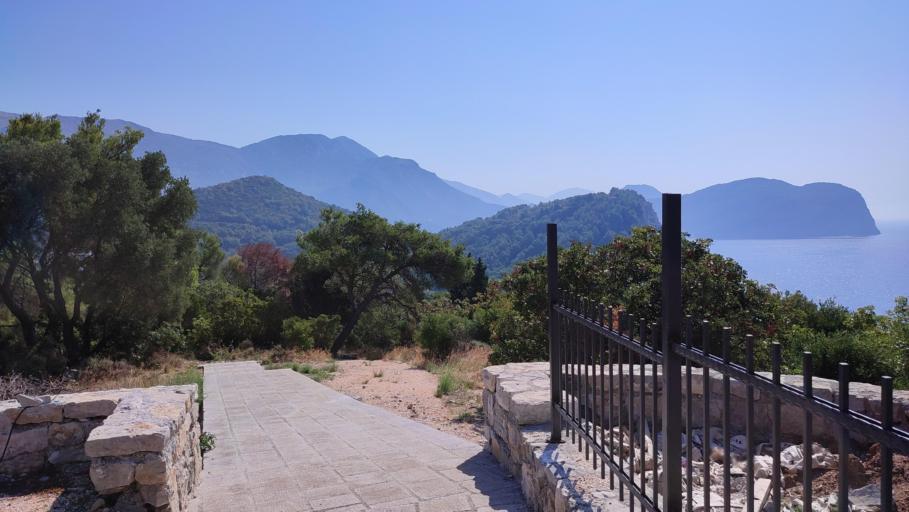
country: ME
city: Petrovac na Moru
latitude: 42.2016
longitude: 18.9459
